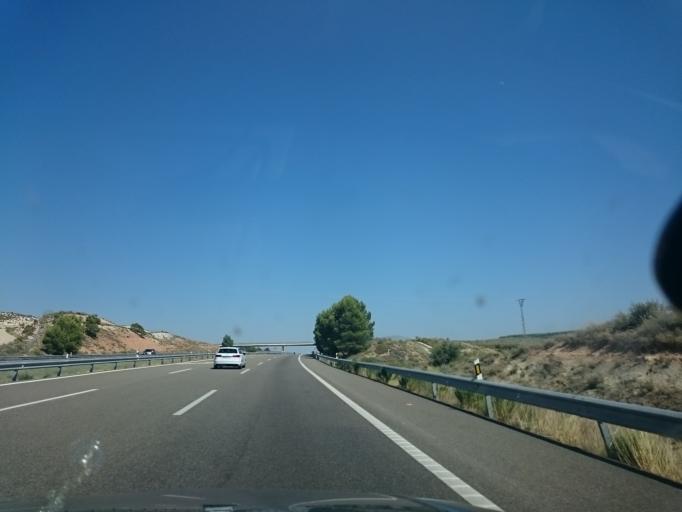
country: ES
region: Aragon
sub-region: Provincia de Huesca
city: Penalba
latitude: 41.5128
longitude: -0.0224
